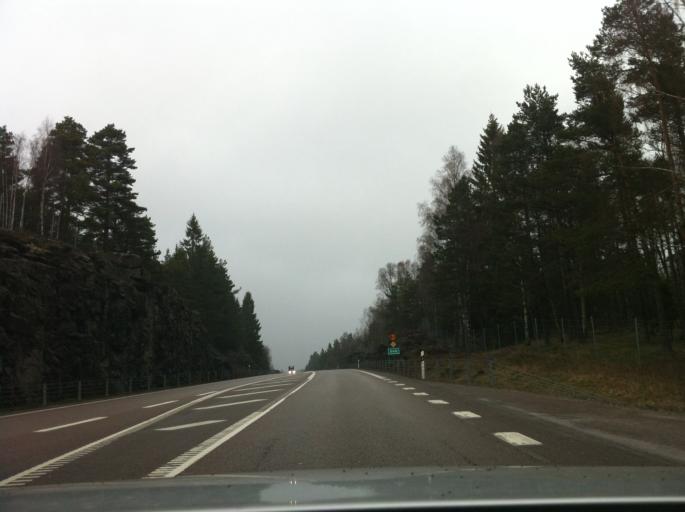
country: SE
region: Vaestra Goetaland
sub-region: Vanersborgs Kommun
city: Vanersborg
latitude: 58.4241
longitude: 12.2900
